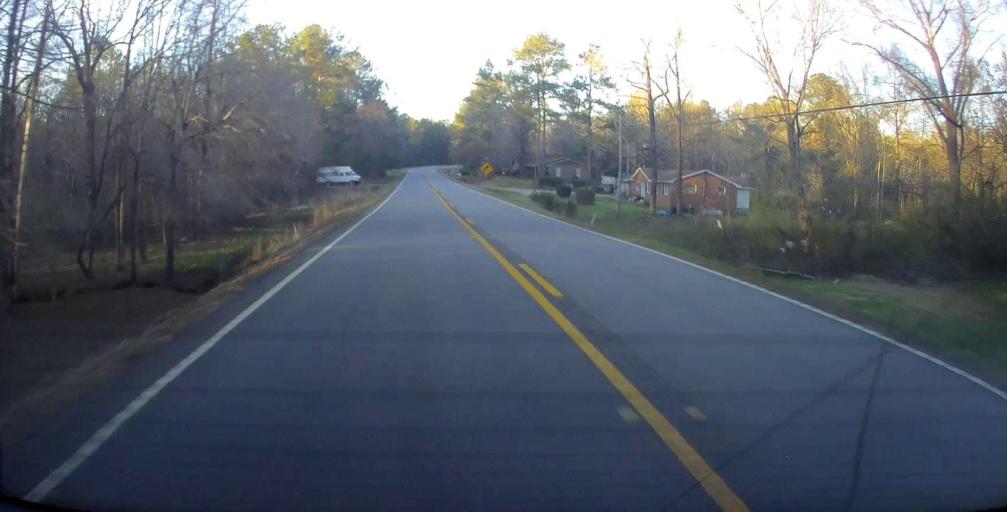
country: US
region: Alabama
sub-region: Lee County
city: Smiths Station
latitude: 32.6309
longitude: -85.0339
